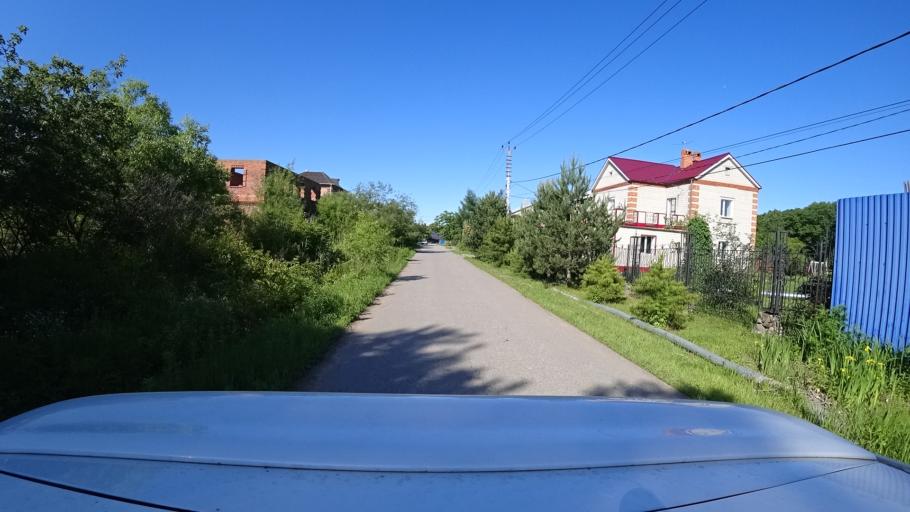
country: RU
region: Khabarovsk Krai
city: Topolevo
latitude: 48.5445
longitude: 135.1789
